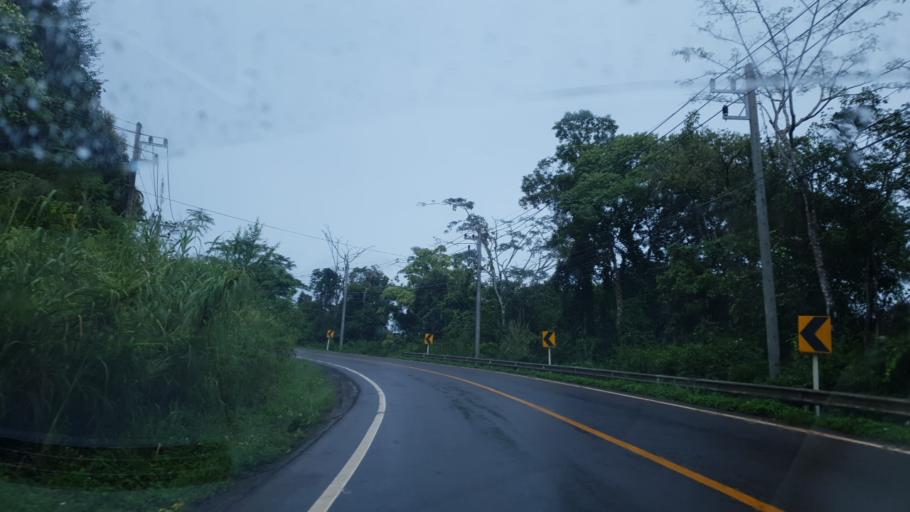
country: TH
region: Mae Hong Son
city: Ban Huai I Huak
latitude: 18.1363
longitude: 98.0769
